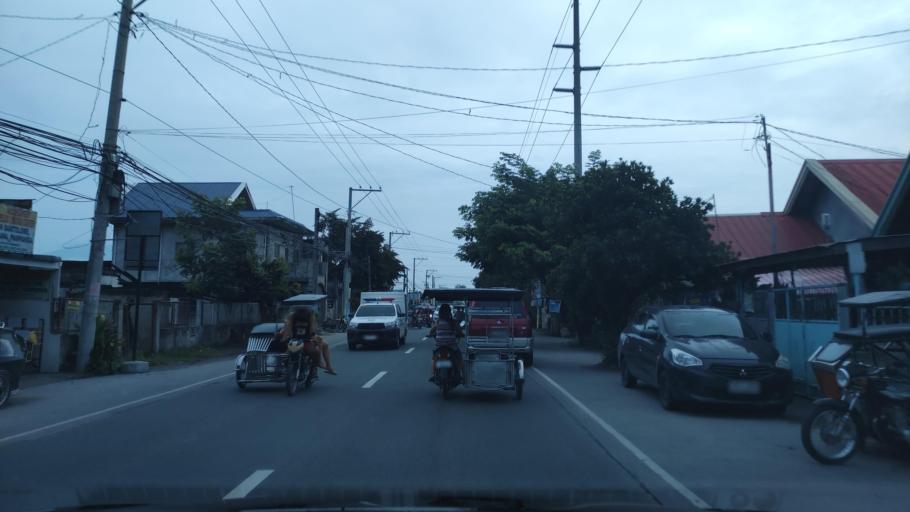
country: PH
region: Central Luzon
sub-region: Province of Pampanga
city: Santa Ana
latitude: 15.1035
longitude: 120.7707
